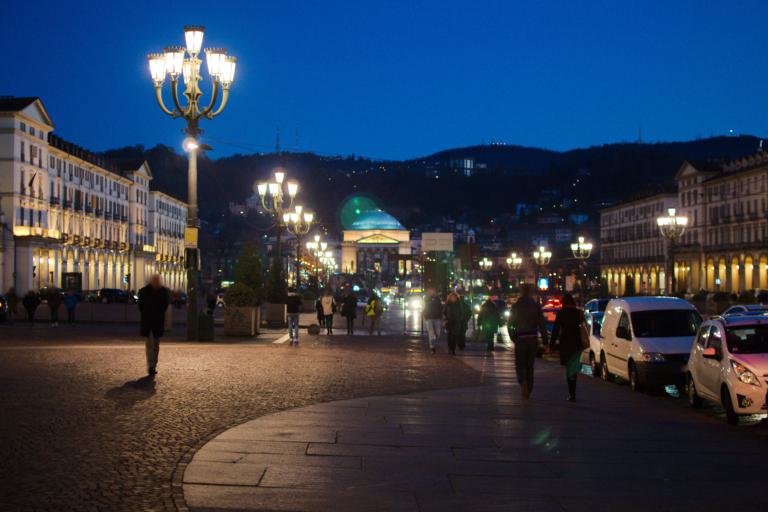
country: IT
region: Piedmont
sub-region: Provincia di Torino
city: Turin
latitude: 45.0658
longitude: 7.6942
